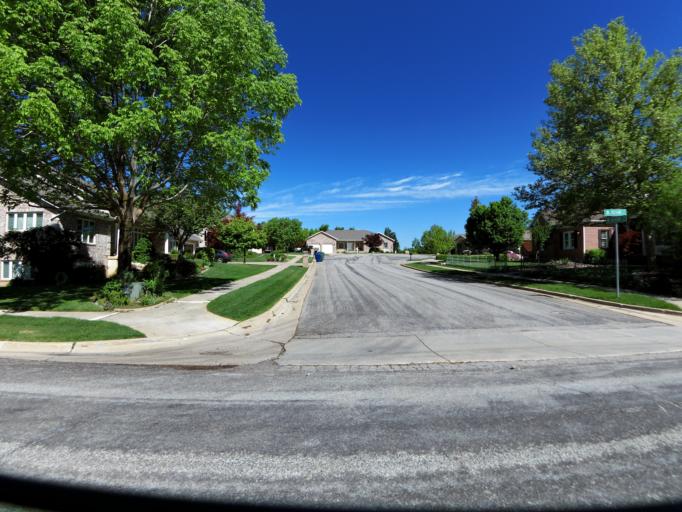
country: US
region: Utah
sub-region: Weber County
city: Uintah
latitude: 41.1663
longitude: -111.9333
